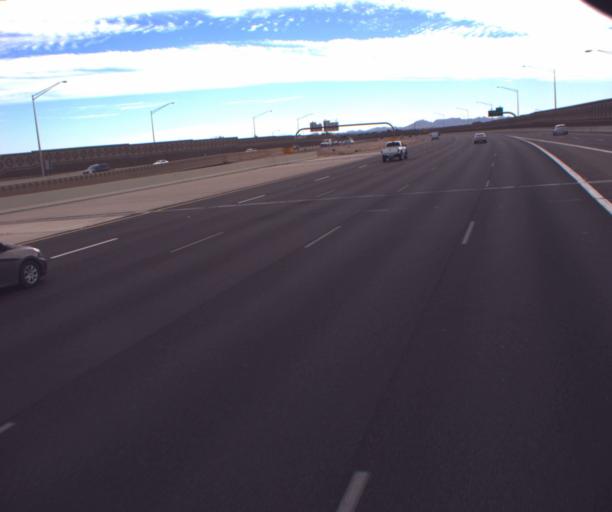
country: US
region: Arizona
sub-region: Pinal County
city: Apache Junction
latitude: 33.3797
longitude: -111.6489
